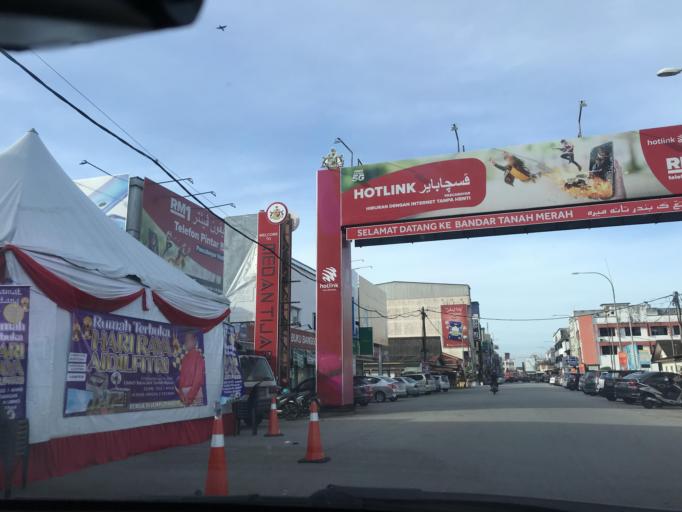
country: MY
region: Kelantan
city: Tanah Merah
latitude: 5.8096
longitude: 102.1487
